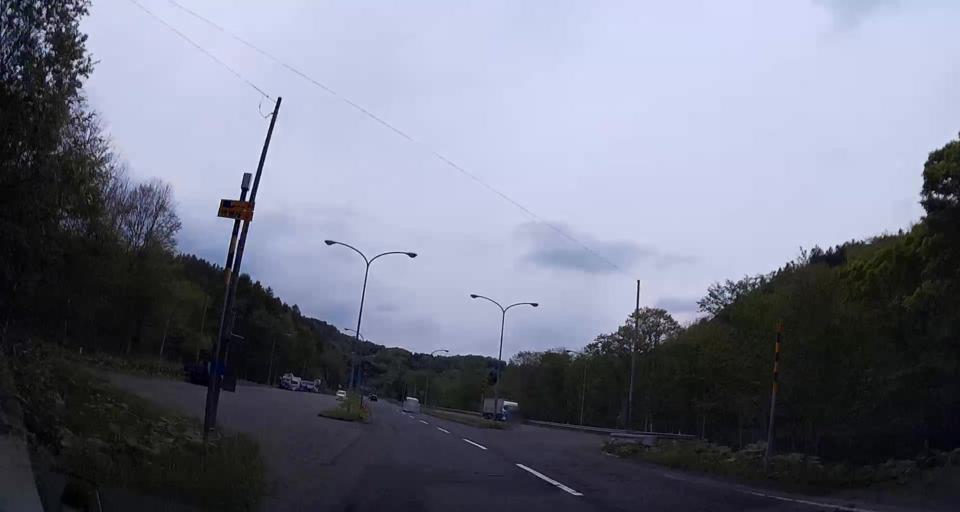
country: JP
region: Hokkaido
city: Shiraoi
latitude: 42.6931
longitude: 141.1062
